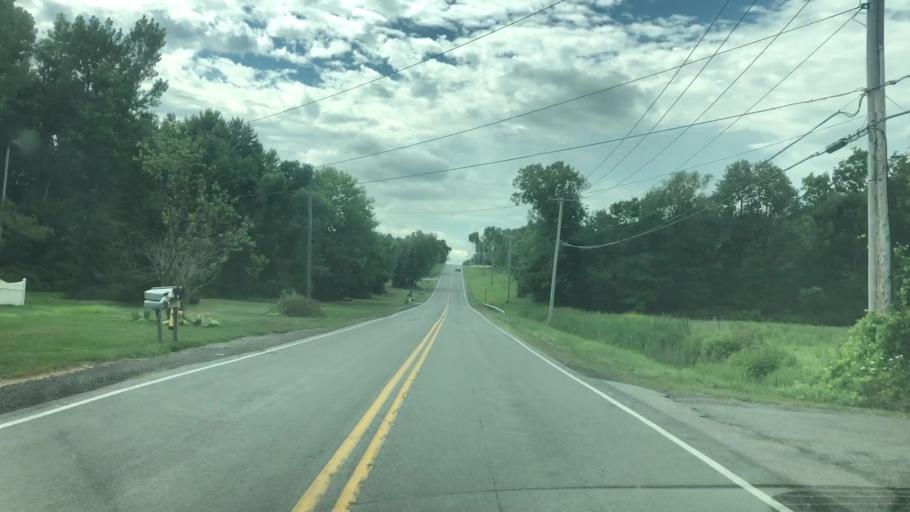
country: US
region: New York
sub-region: Monroe County
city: Fairport
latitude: 43.0731
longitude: -77.3922
